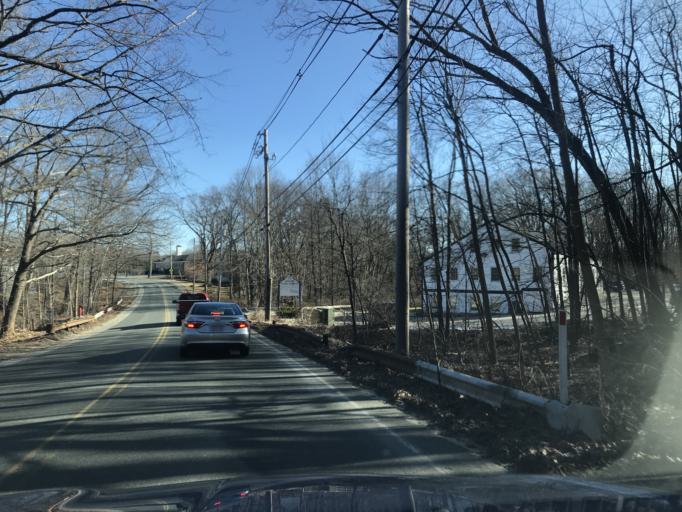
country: US
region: Massachusetts
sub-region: Essex County
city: North Andover
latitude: 42.7066
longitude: -71.0703
